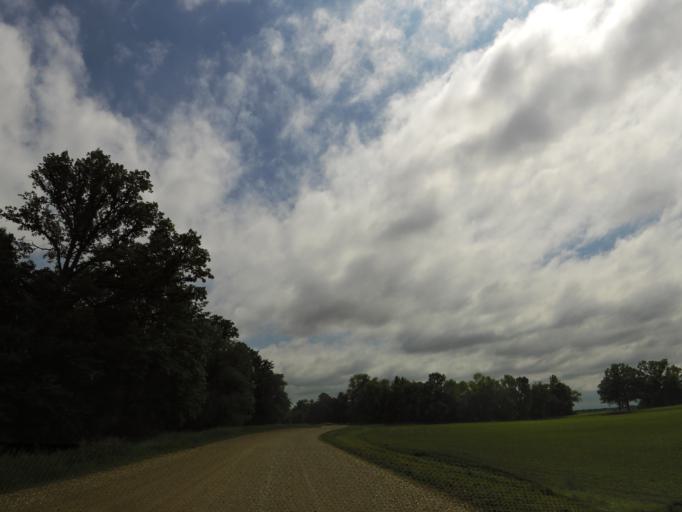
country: US
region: North Dakota
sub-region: Walsh County
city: Grafton
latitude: 48.4220
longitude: -97.4919
